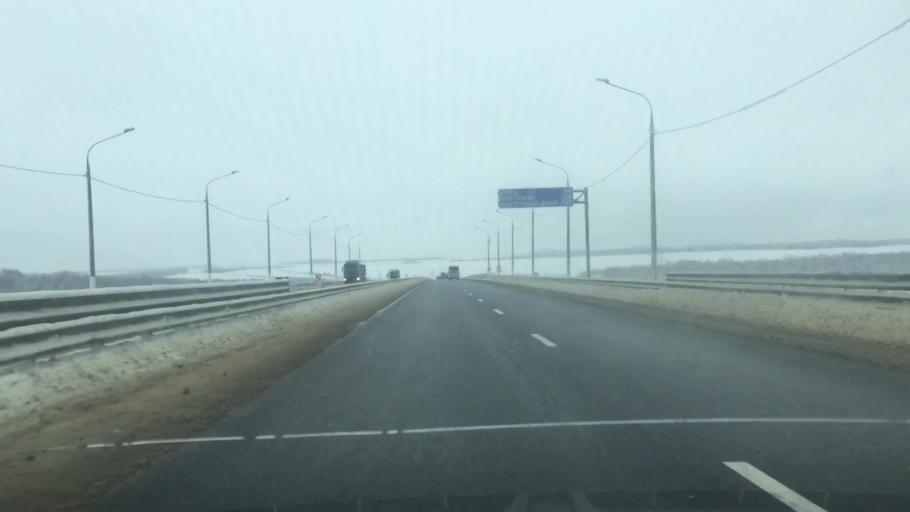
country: RU
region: Tula
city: Kazachka
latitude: 53.2879
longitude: 38.1788
